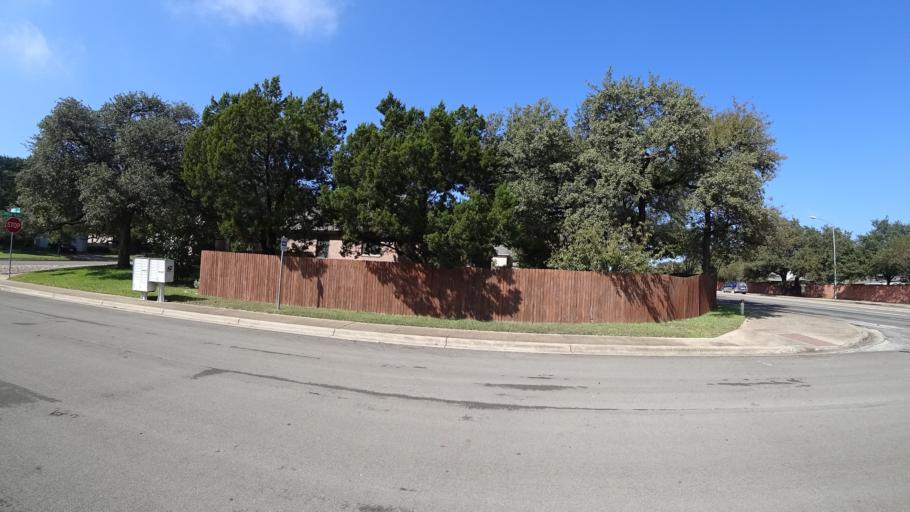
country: US
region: Texas
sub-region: Travis County
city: Shady Hollow
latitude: 30.2084
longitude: -97.8711
